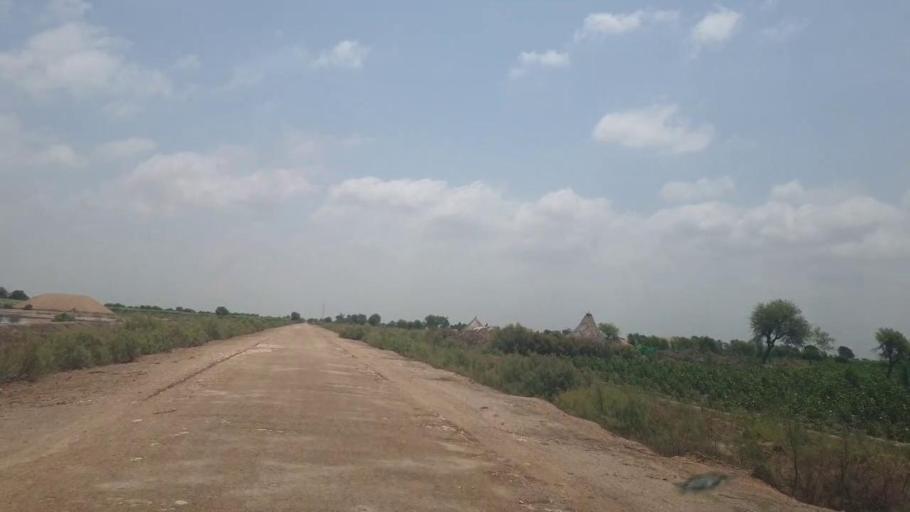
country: PK
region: Sindh
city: Tando Mittha Khan
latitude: 25.9180
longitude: 69.2040
